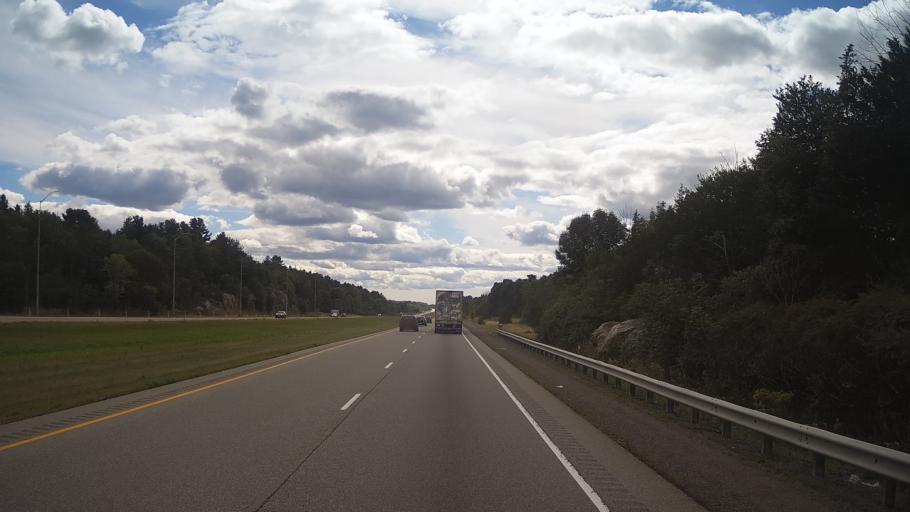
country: CA
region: Ontario
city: Brockville
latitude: 44.5040
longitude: -75.8394
